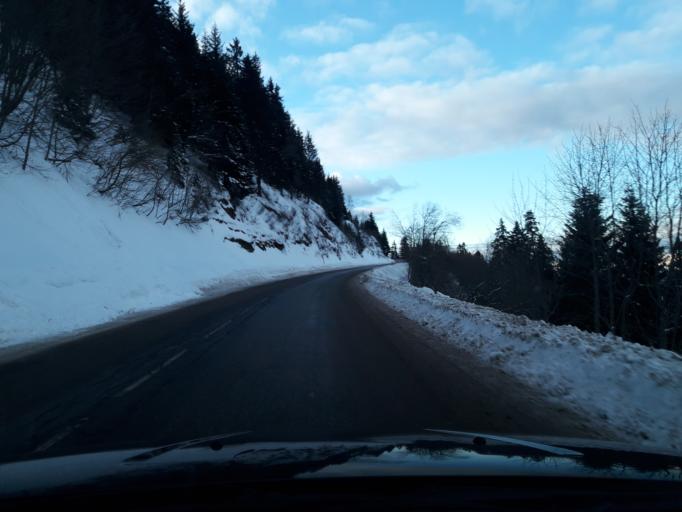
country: FR
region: Rhone-Alpes
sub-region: Departement de l'Isere
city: Vaulnaveys-le-Bas
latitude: 45.1227
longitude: 5.8776
